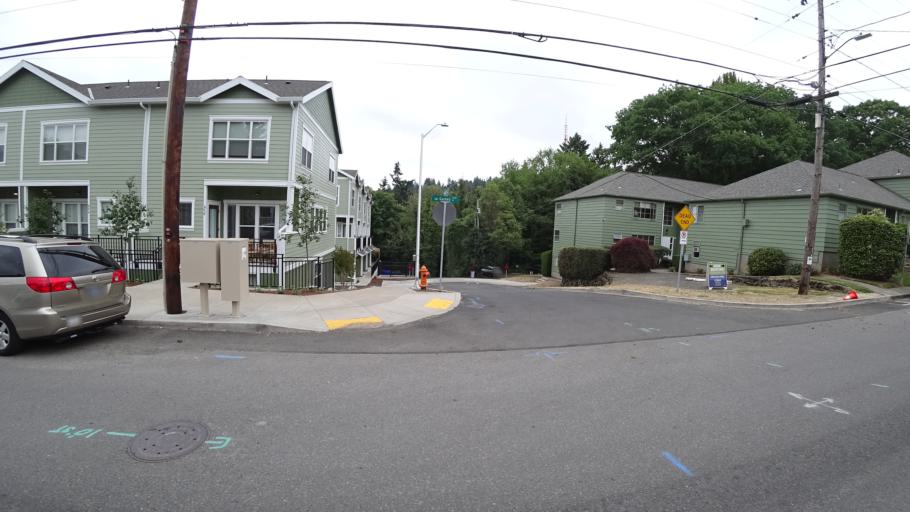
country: US
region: Oregon
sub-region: Multnomah County
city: Portland
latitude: 45.4969
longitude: -122.6903
